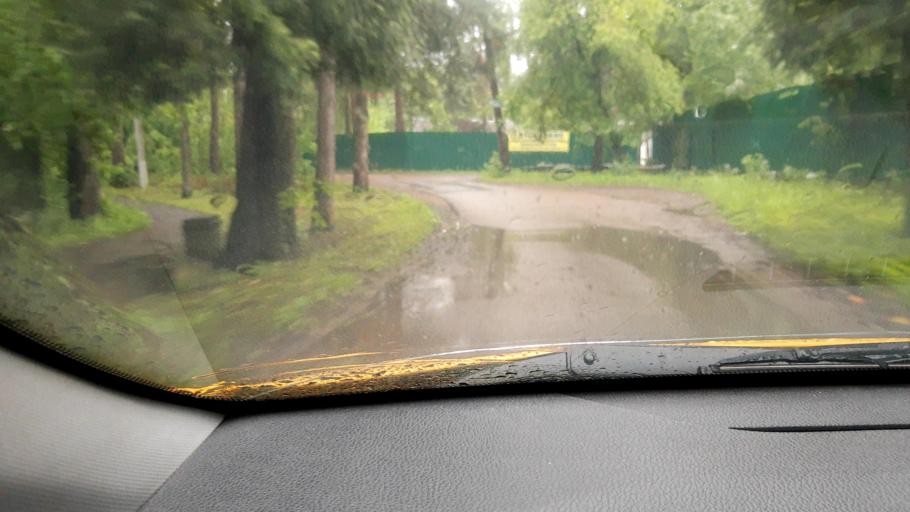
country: RU
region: Moskovskaya
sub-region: Podol'skiy Rayon
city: Podol'sk
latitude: 55.4123
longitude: 37.6119
